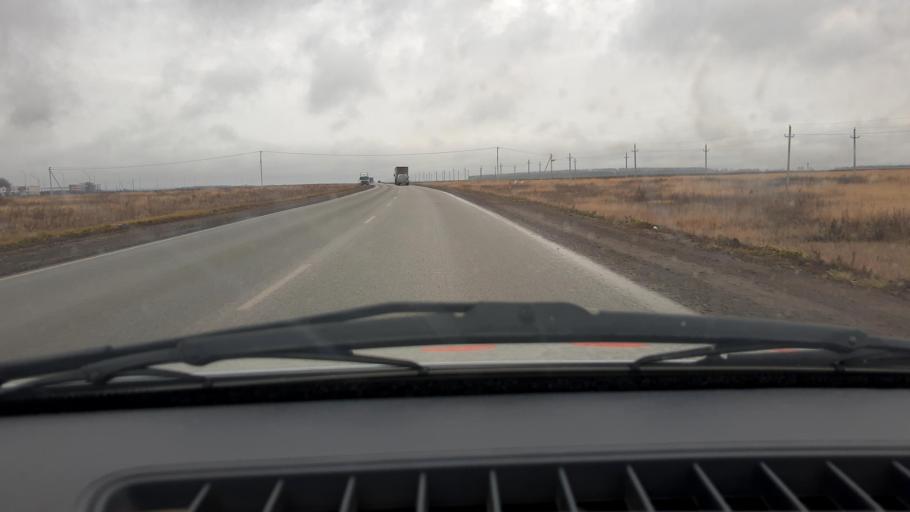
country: RU
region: Bashkortostan
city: Iglino
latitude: 54.7640
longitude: 56.2659
